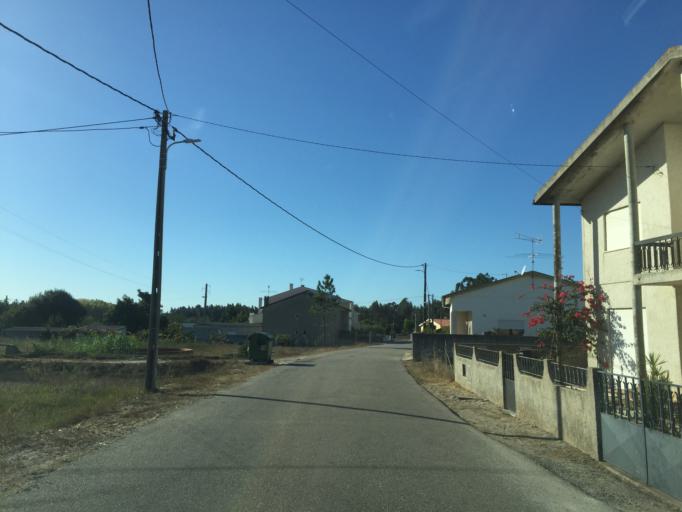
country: PT
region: Coimbra
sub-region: Figueira da Foz
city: Tavarede
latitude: 40.2173
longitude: -8.8533
